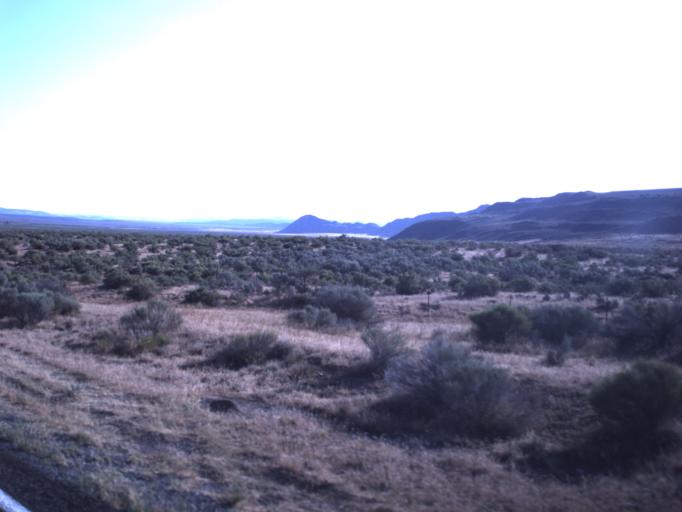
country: US
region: Utah
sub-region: Iron County
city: Enoch
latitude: 37.8585
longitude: -113.0316
